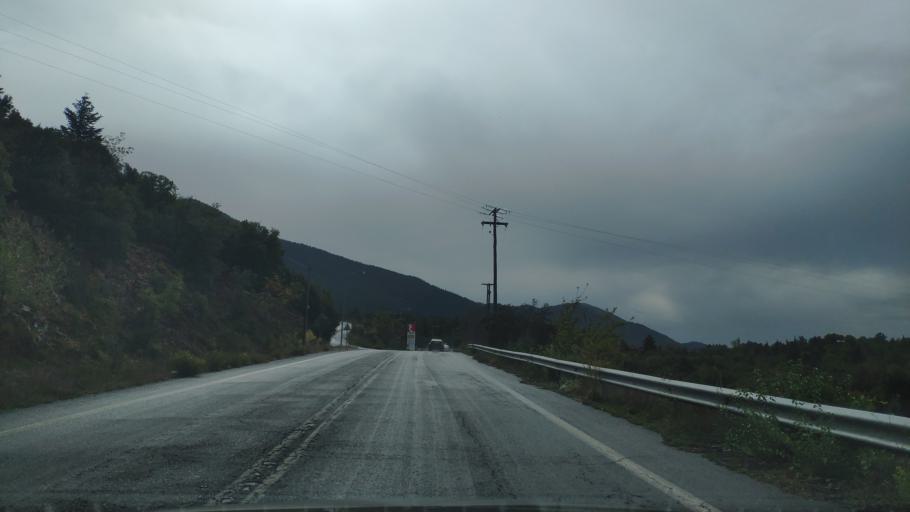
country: GR
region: Peloponnese
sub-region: Nomos Arkadias
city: Langadhia
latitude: 37.6826
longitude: 22.1911
